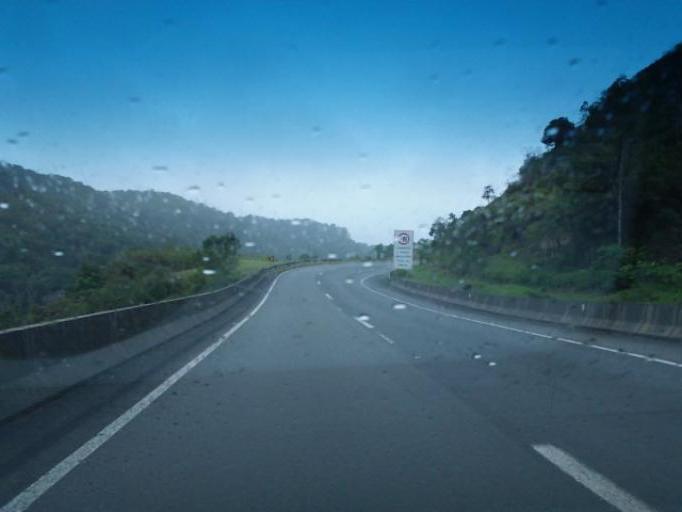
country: BR
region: Sao Paulo
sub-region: Cajati
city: Cajati
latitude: -24.9664
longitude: -48.4613
